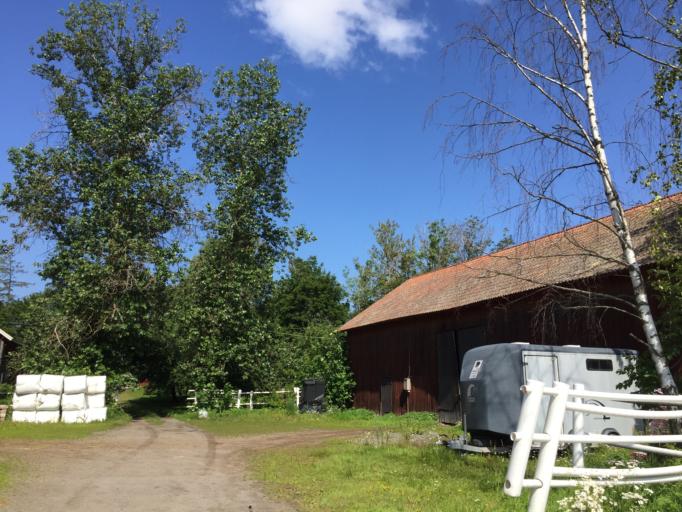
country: SE
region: Uppsala
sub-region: Enkopings Kommun
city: Hummelsta
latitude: 59.6176
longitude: 16.9038
